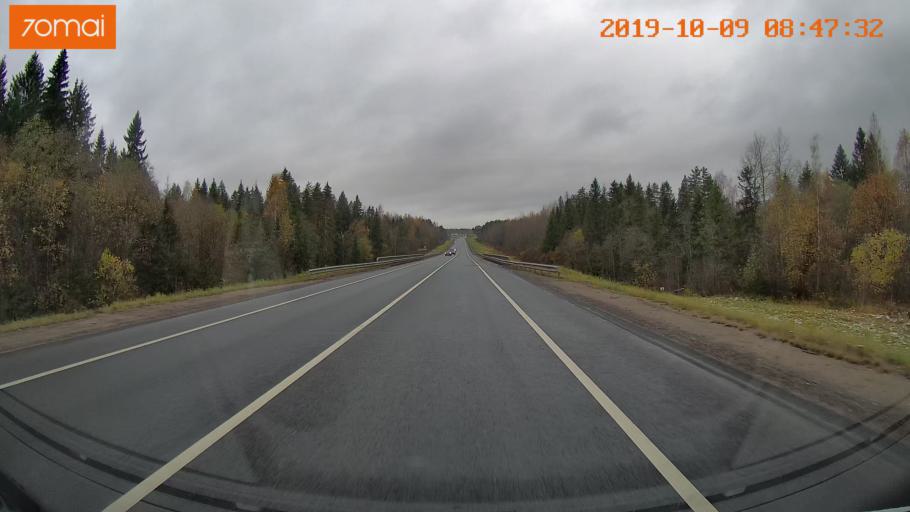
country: RU
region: Vologda
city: Vologda
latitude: 59.0657
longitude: 40.0447
